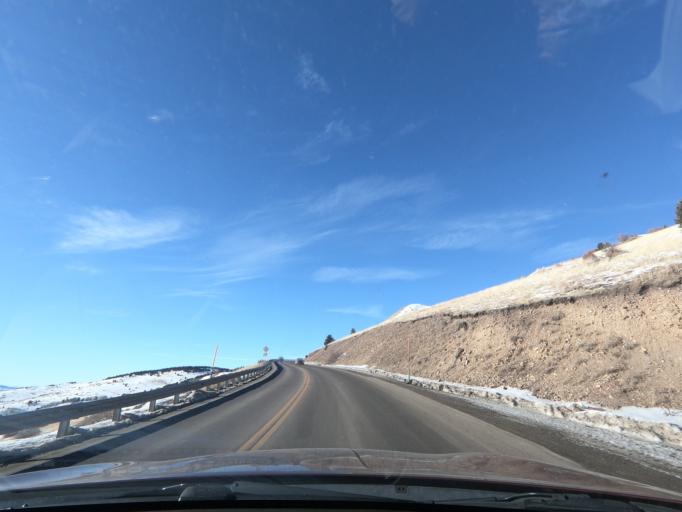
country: US
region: Colorado
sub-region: Teller County
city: Cripple Creek
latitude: 38.7543
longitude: -105.1614
